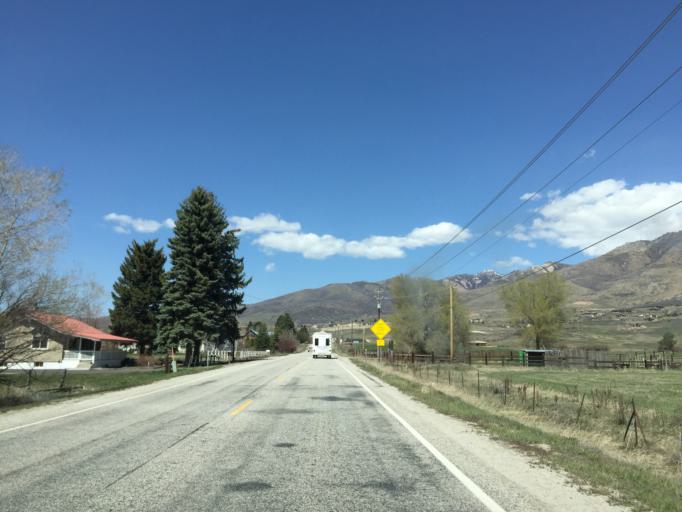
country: US
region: Utah
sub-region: Weber County
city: Wolf Creek
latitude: 41.3071
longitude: -111.8253
